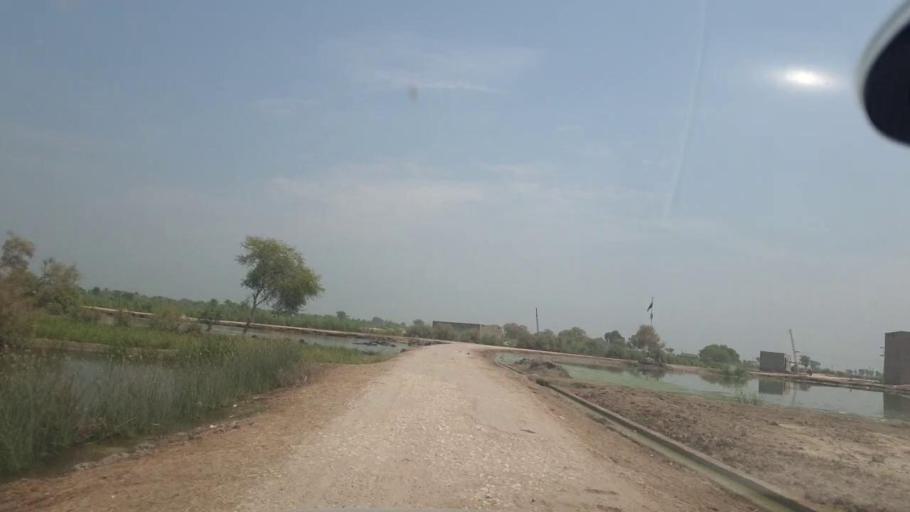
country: PK
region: Sindh
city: Thul
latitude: 28.1712
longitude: 68.6382
